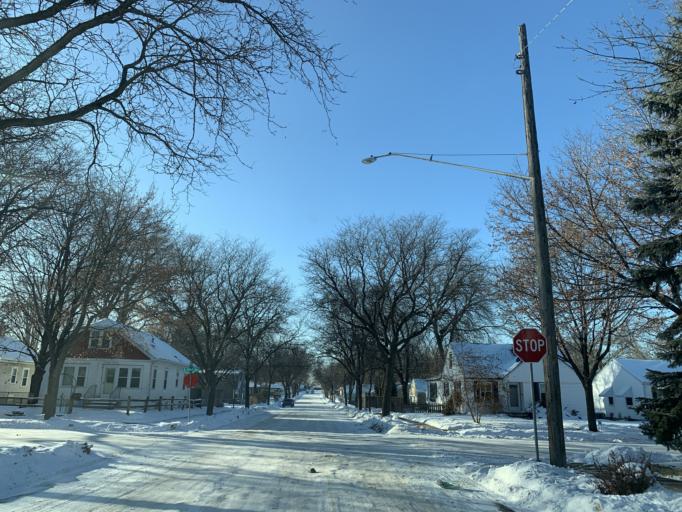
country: US
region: Minnesota
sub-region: Hennepin County
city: Richfield
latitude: 44.8999
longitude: -93.2138
